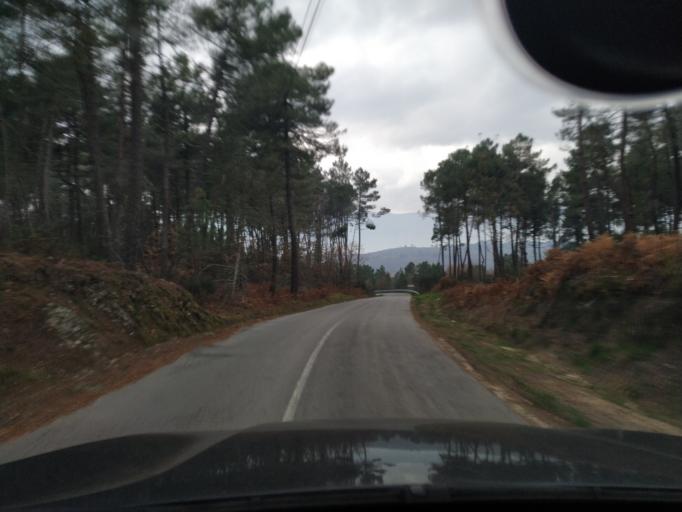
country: PT
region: Vila Real
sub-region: Vila Real
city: Vila Real
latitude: 41.3376
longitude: -7.6556
